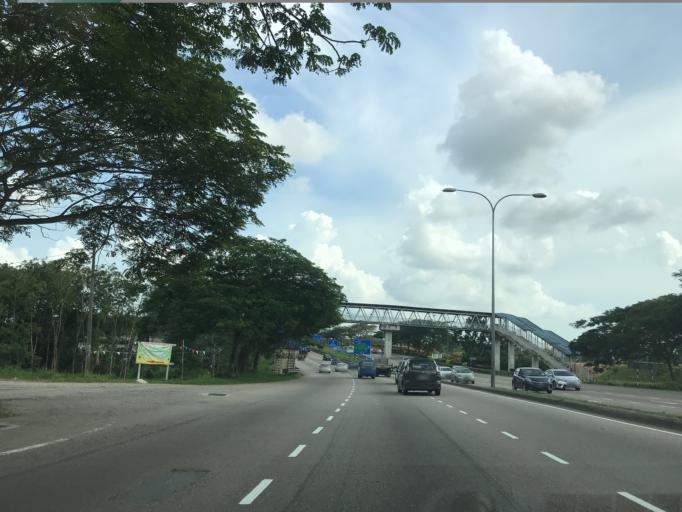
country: MY
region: Johor
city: Taman Senai
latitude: 1.5849
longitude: 103.6497
